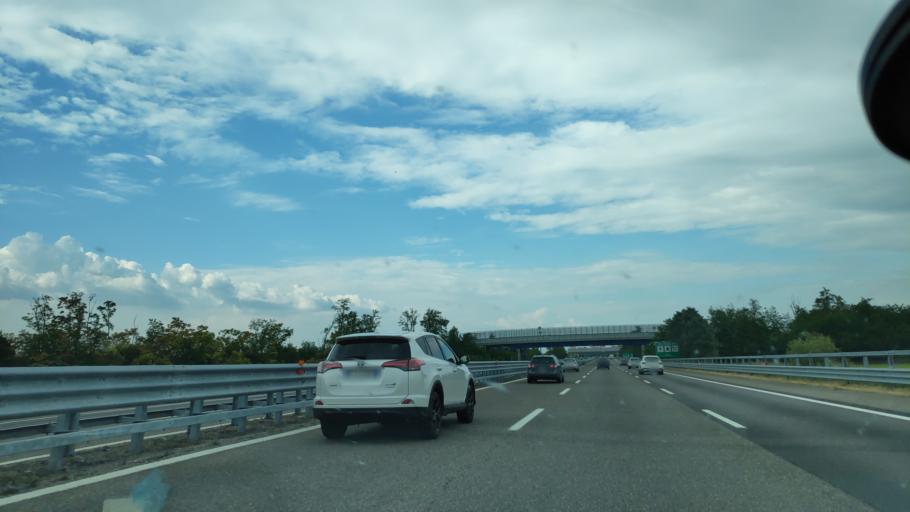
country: IT
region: Lombardy
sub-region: Provincia di Pavia
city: Gropello Cairoli
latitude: 45.1414
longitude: 8.9874
